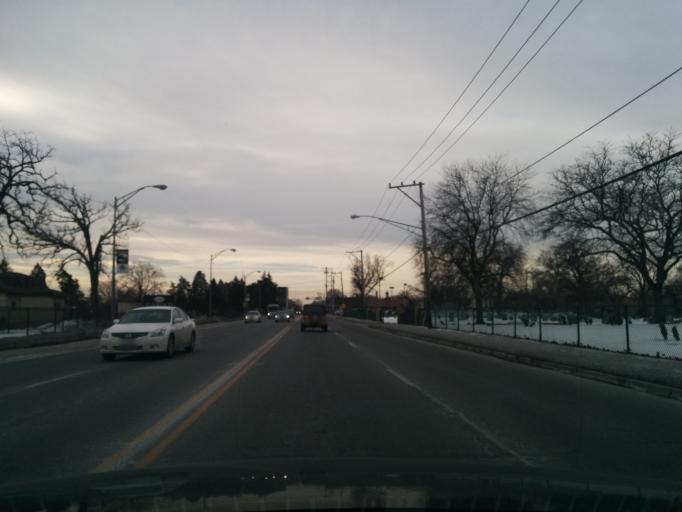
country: US
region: Illinois
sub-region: Cook County
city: River Grove
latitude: 41.9331
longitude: -87.8359
